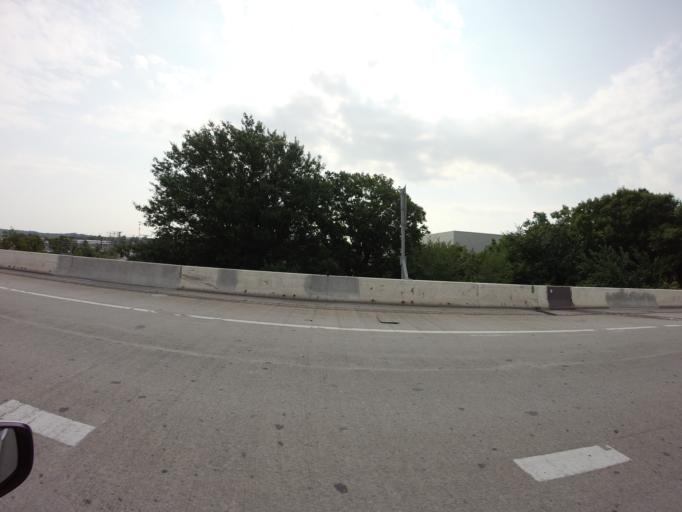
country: US
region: Maryland
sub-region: Baltimore County
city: Rosedale
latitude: 39.2950
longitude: -76.5312
